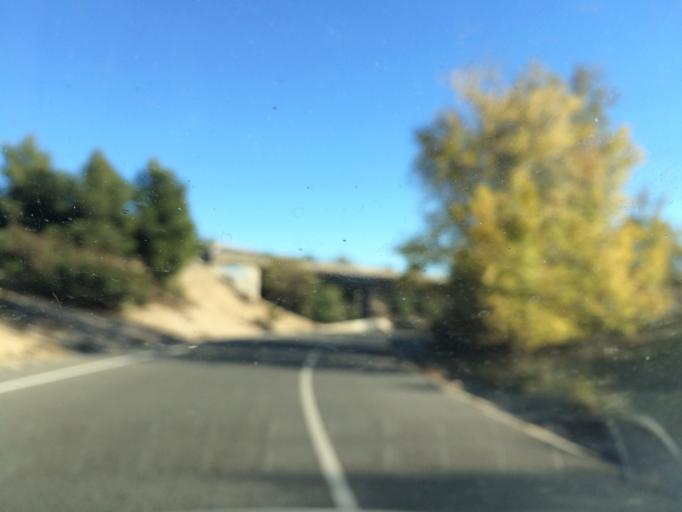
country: ES
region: Madrid
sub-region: Provincia de Madrid
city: Las Tablas
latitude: 40.5090
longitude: -3.6601
